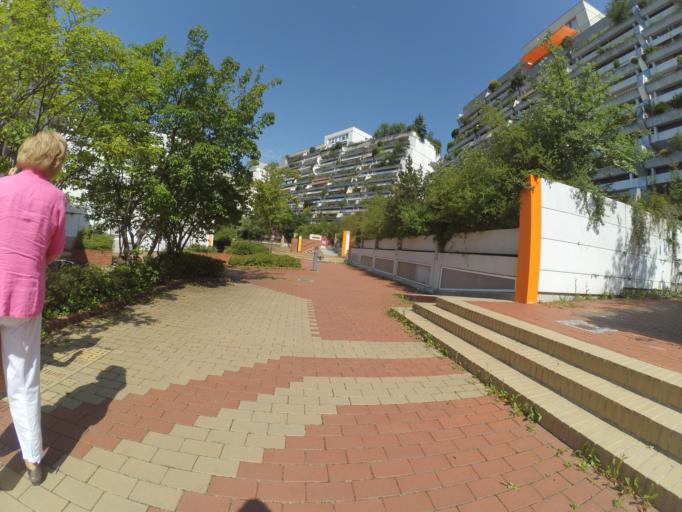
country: DE
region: Bavaria
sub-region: Upper Bavaria
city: Munich
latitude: 48.1848
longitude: 11.5501
